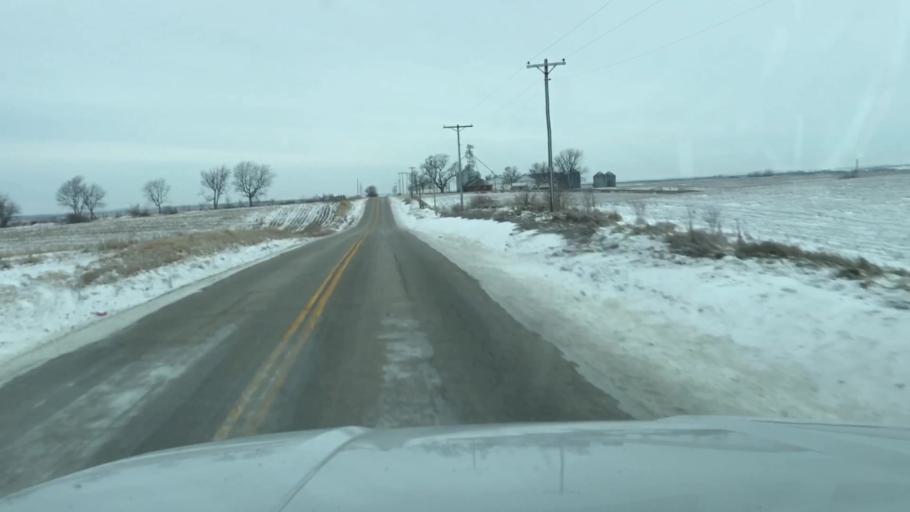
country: US
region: Missouri
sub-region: Andrew County
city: Savannah
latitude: 40.0248
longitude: -94.9334
